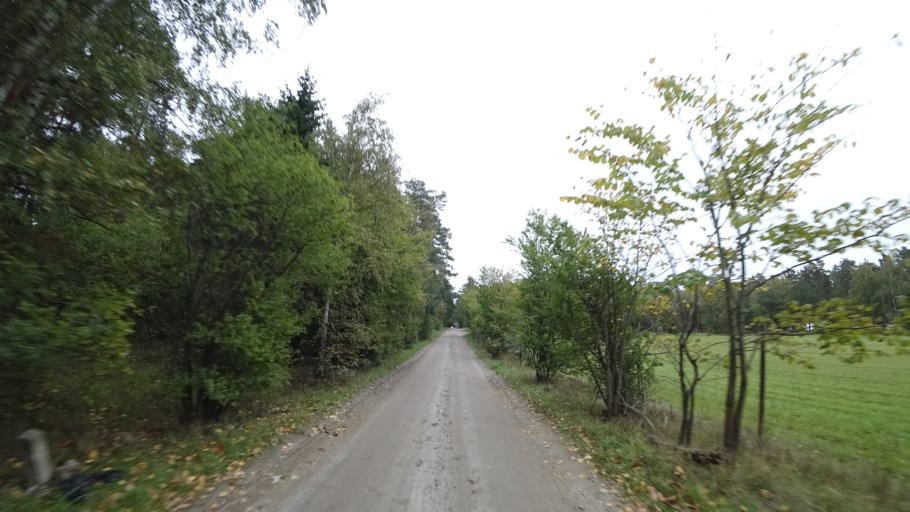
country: SE
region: Skane
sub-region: Kavlinge Kommun
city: Hofterup
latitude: 55.8232
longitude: 12.9640
